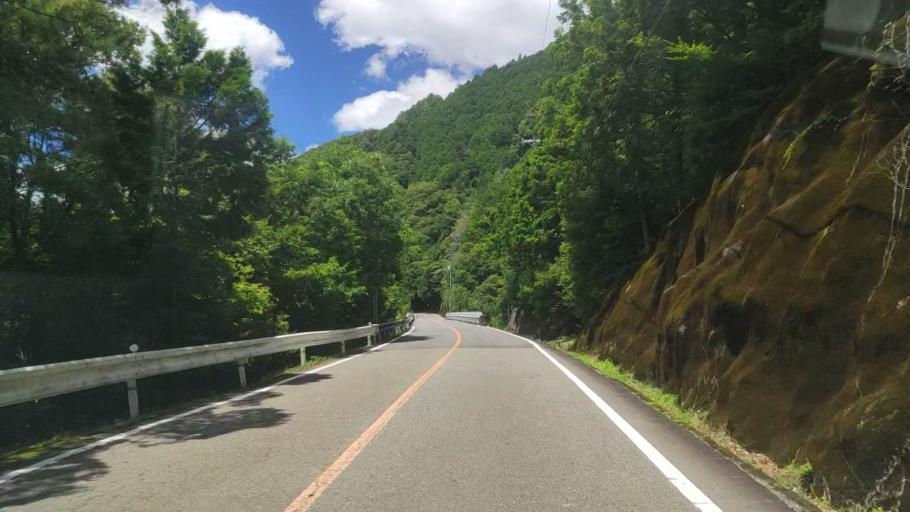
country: JP
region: Mie
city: Owase
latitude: 33.9970
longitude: 136.0235
